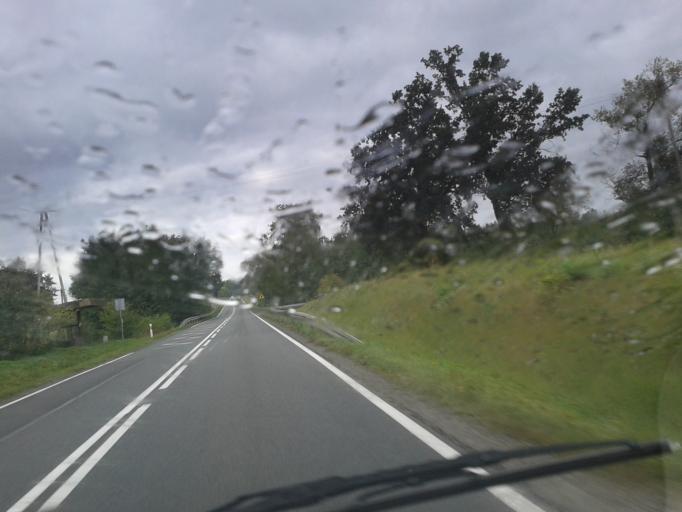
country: PL
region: Kujawsko-Pomorskie
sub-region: Powiat sepolenski
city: Sepolno Krajenskie
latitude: 53.4856
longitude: 17.5185
